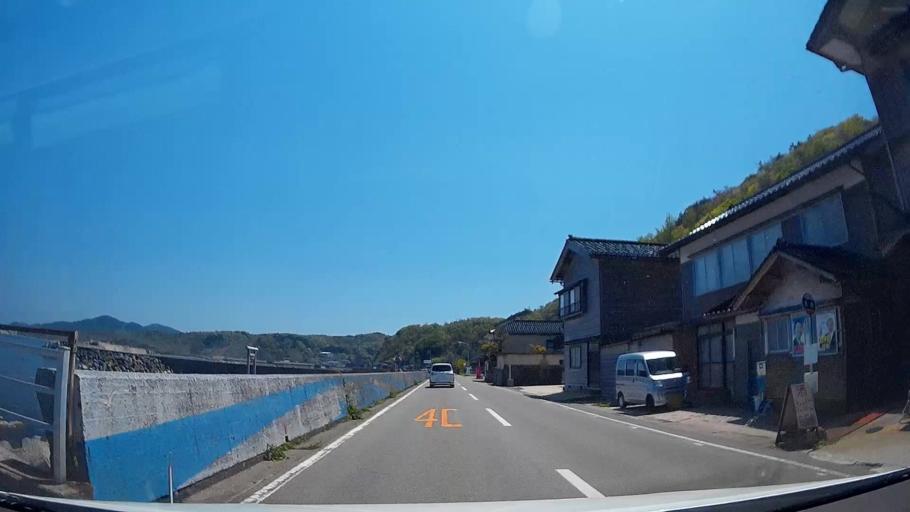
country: JP
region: Ishikawa
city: Nanao
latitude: 37.4328
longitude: 137.0196
